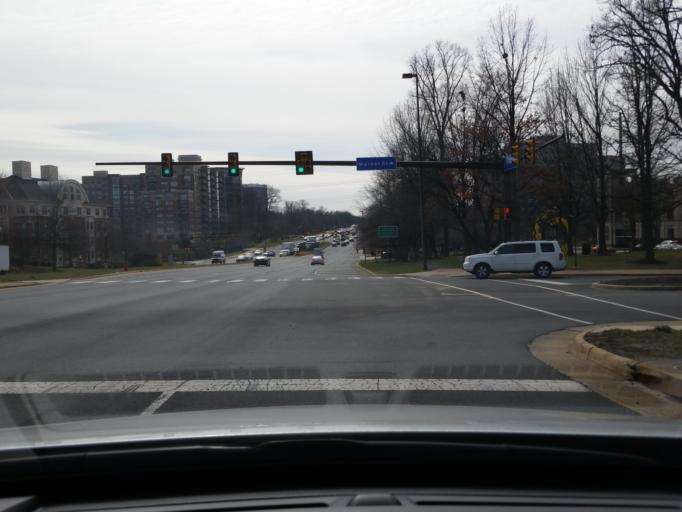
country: US
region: Virginia
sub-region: Fairfax County
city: Reston
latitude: 38.9590
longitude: -77.3547
